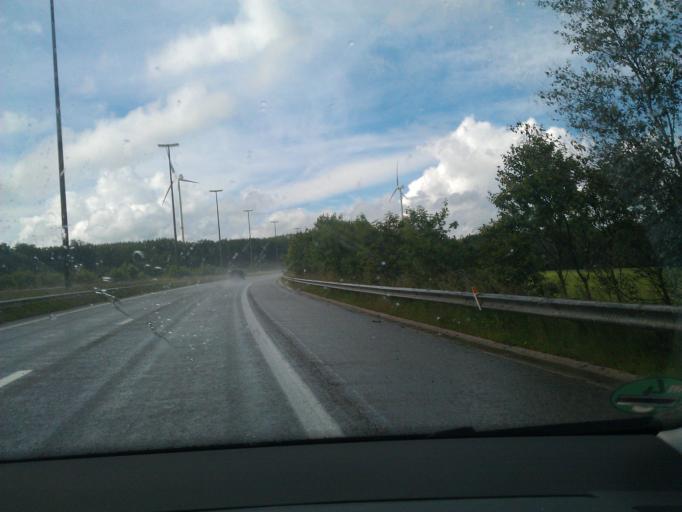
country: BE
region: Wallonia
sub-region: Province de Liege
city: Saint-Vith
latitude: 50.2978
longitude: 6.0820
